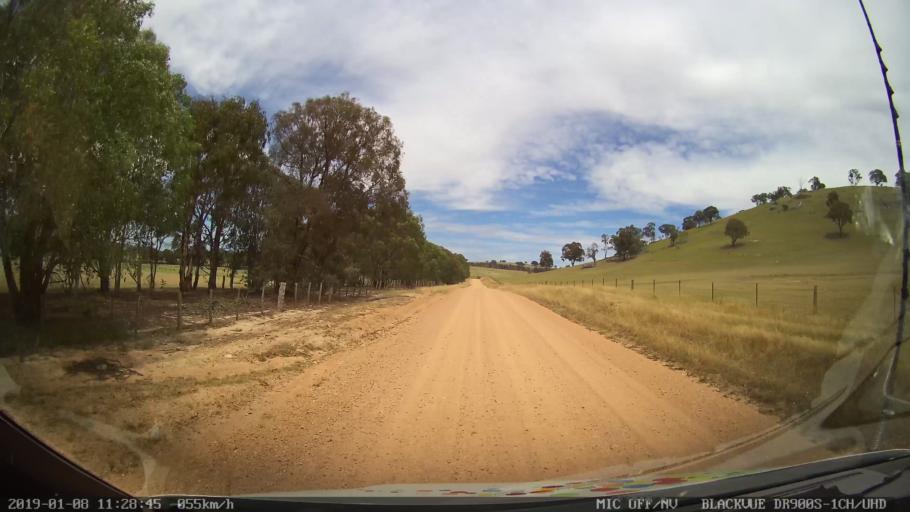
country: AU
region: New South Wales
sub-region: Guyra
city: Guyra
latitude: -30.2981
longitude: 151.5532
